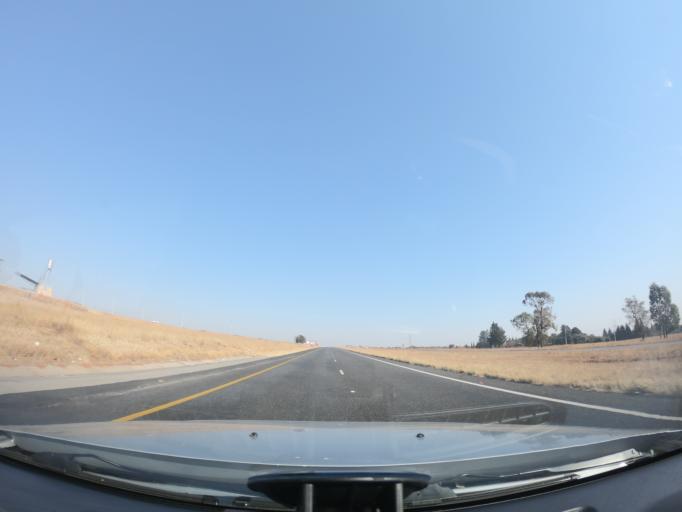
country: ZA
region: Gauteng
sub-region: City of Tshwane Metropolitan Municipality
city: Cullinan
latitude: -25.7977
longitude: 28.5166
